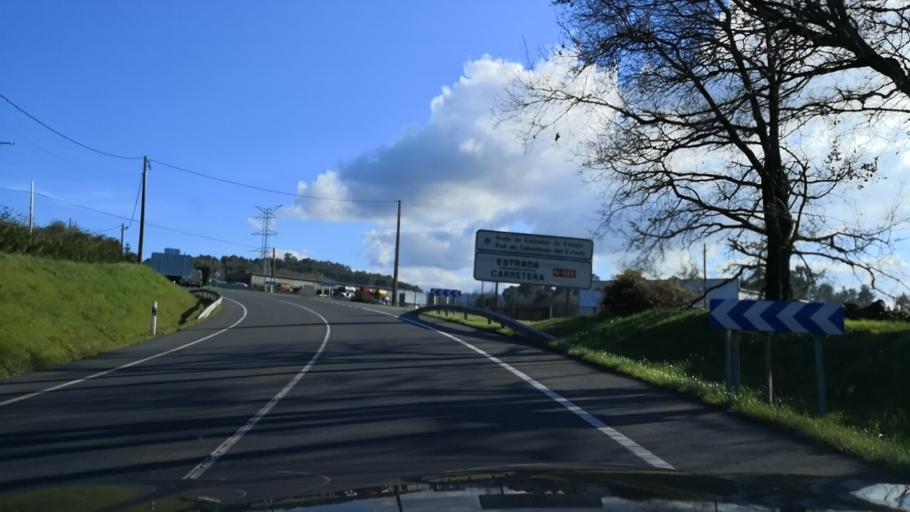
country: ES
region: Galicia
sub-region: Provincia de Pontevedra
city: Silleda
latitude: 42.7137
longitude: -8.2798
